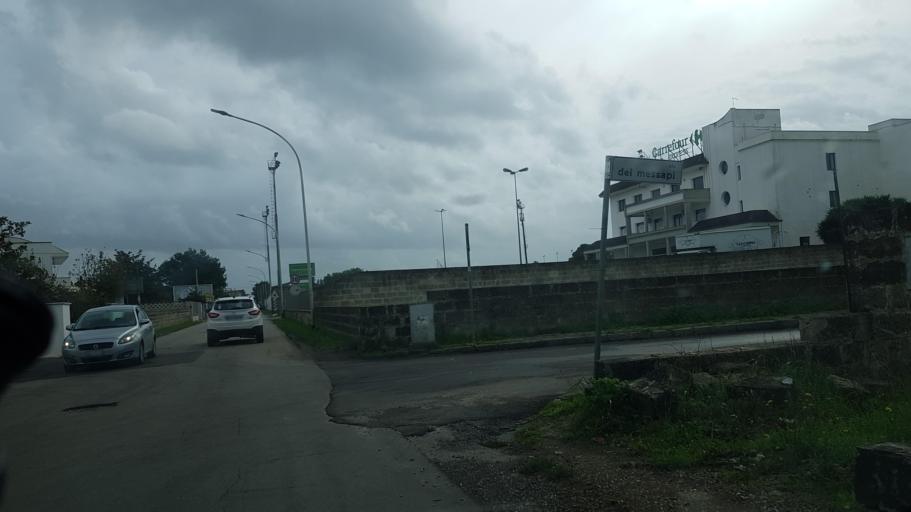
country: IT
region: Apulia
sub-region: Provincia di Lecce
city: Carmiano
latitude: 40.3448
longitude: 18.0515
